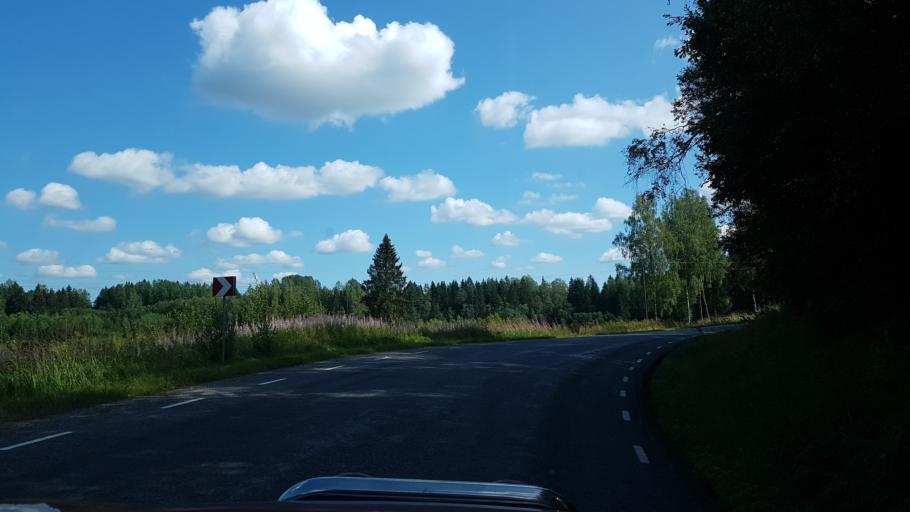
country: EE
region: Vorumaa
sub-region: Voru linn
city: Voru
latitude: 57.7048
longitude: 27.0725
